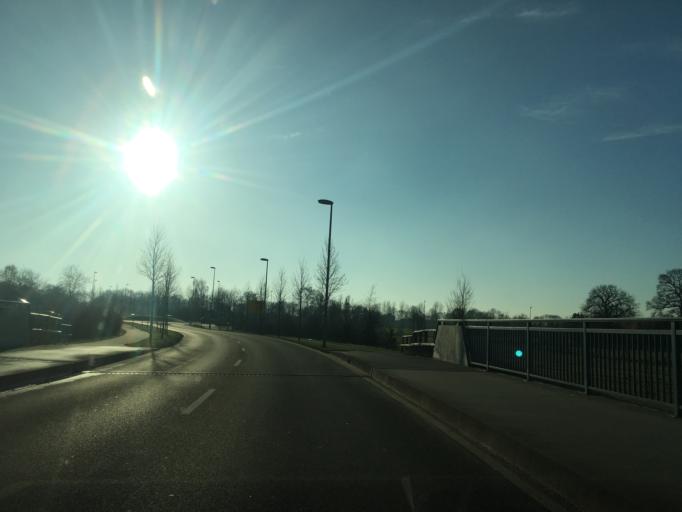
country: DE
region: North Rhine-Westphalia
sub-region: Regierungsbezirk Munster
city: Muenster
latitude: 51.9719
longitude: 7.5883
